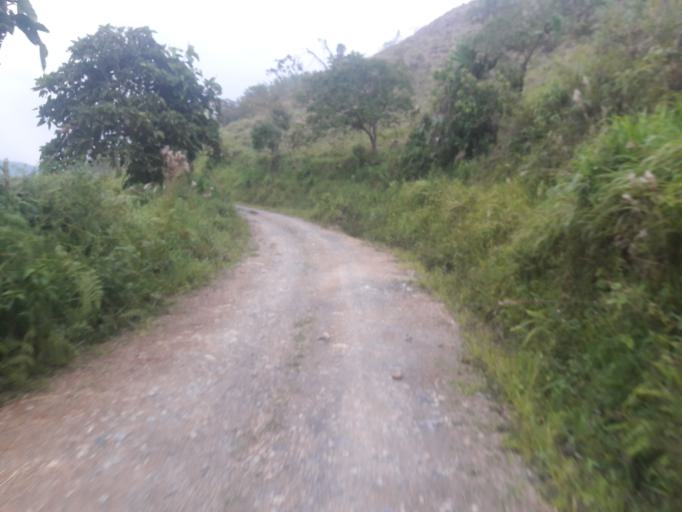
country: CO
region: Boyaca
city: Quipama
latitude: 5.5847
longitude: -74.2208
